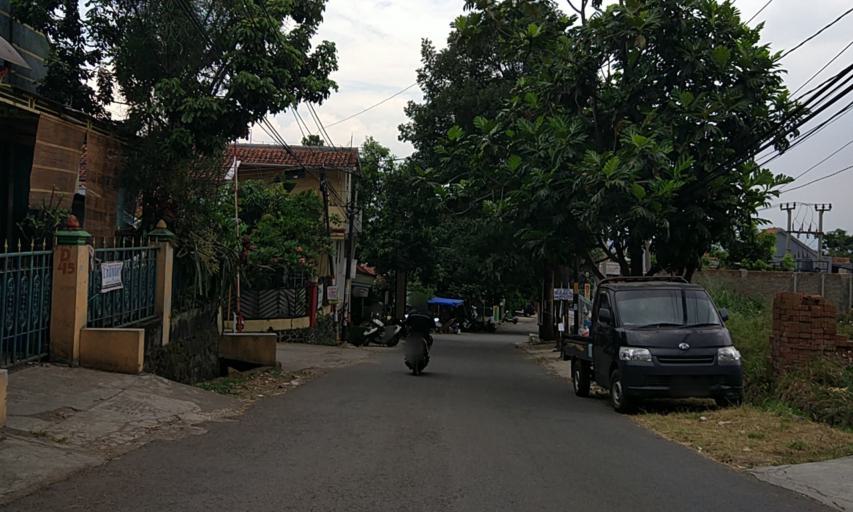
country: ID
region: West Java
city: Cileunyi
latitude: -6.9023
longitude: 107.6979
